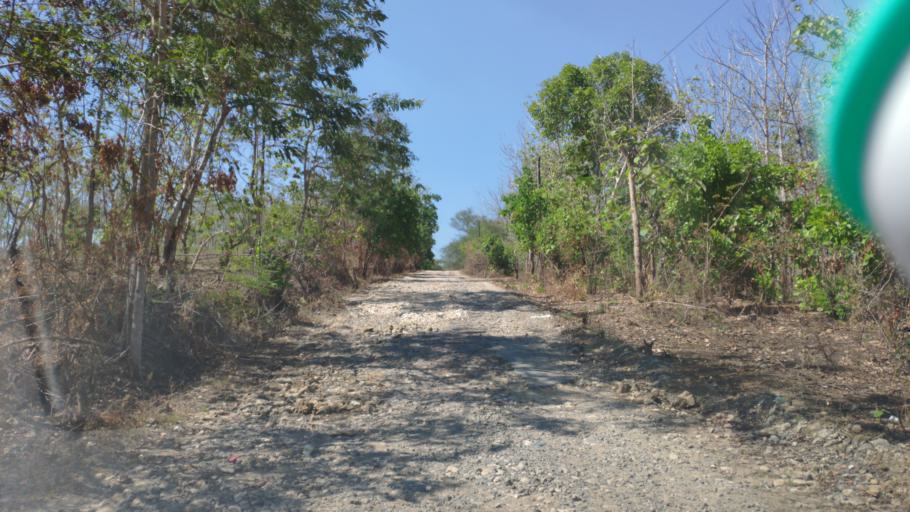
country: ID
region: East Java
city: Kedewan
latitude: -7.0060
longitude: 111.6061
